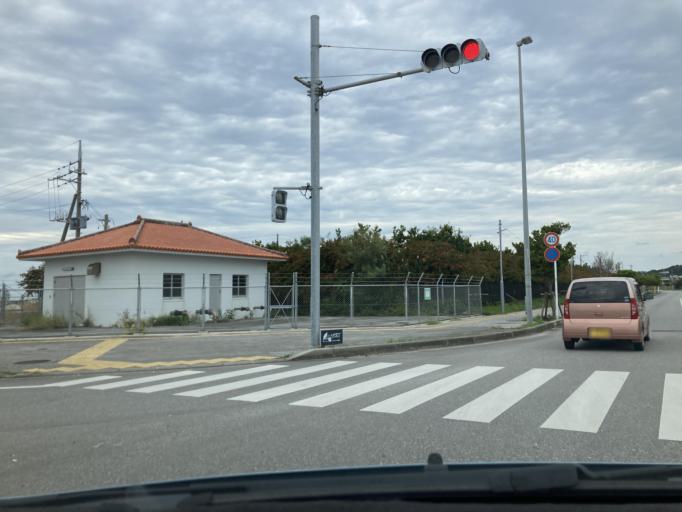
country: JP
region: Okinawa
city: Okinawa
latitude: 26.3935
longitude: 127.7410
